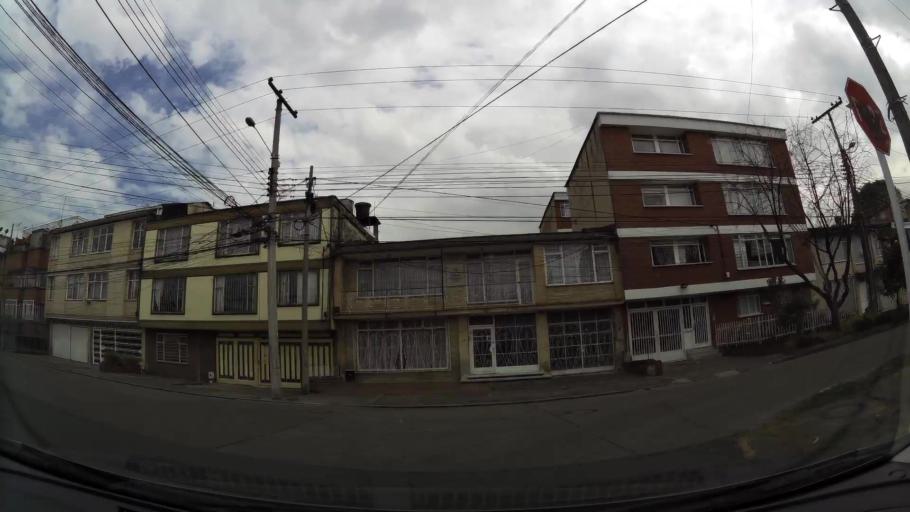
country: CO
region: Bogota D.C.
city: Bogota
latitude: 4.6325
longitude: -74.0768
